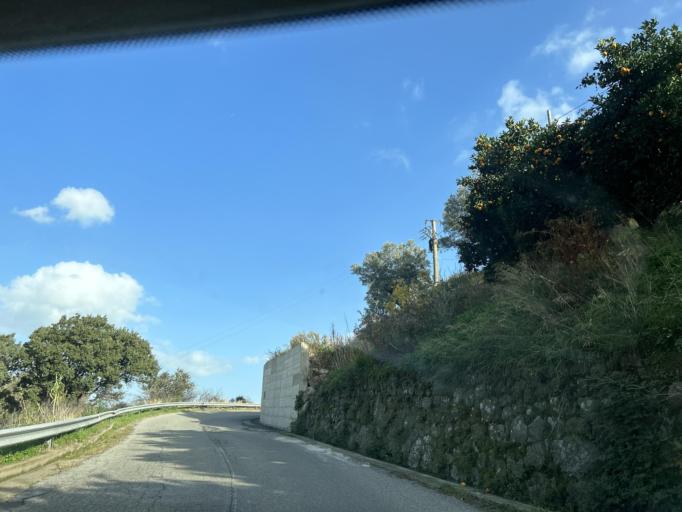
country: IT
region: Calabria
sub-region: Provincia di Catanzaro
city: Montepaone
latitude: 38.7243
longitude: 16.5081
